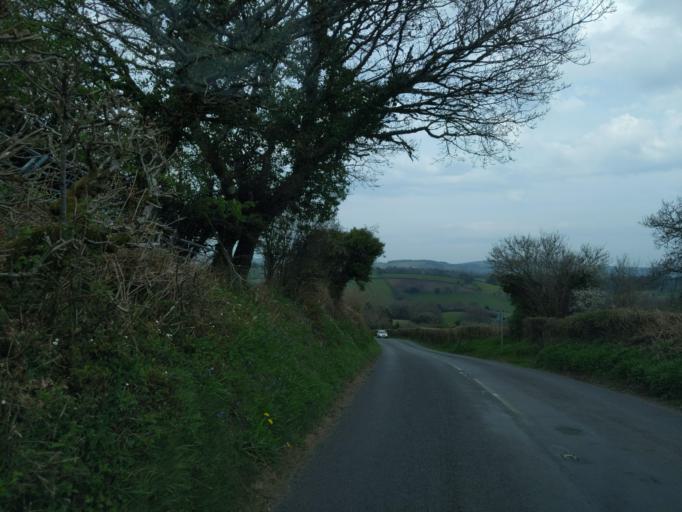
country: GB
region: England
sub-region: Devon
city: Ashburton
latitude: 50.6462
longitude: -3.8201
